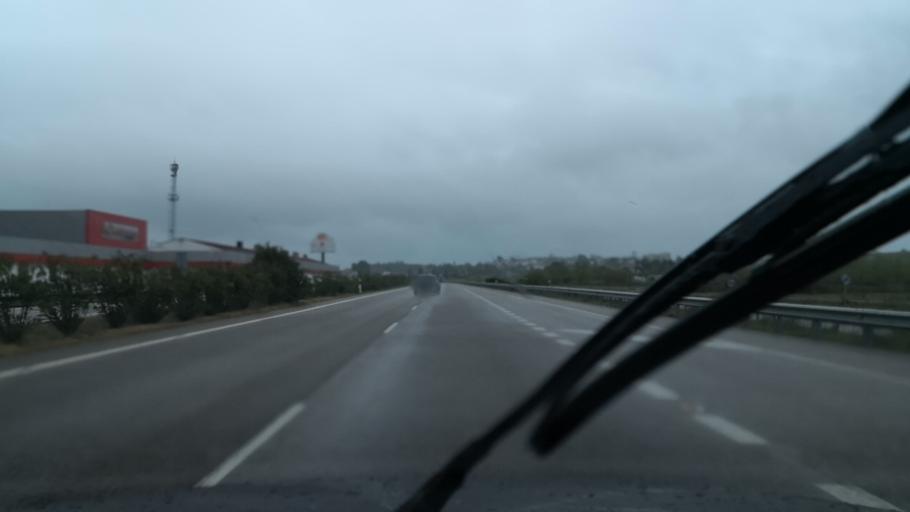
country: ES
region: Extremadura
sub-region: Provincia de Badajoz
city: Badajoz
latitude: 38.9053
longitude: -6.9663
